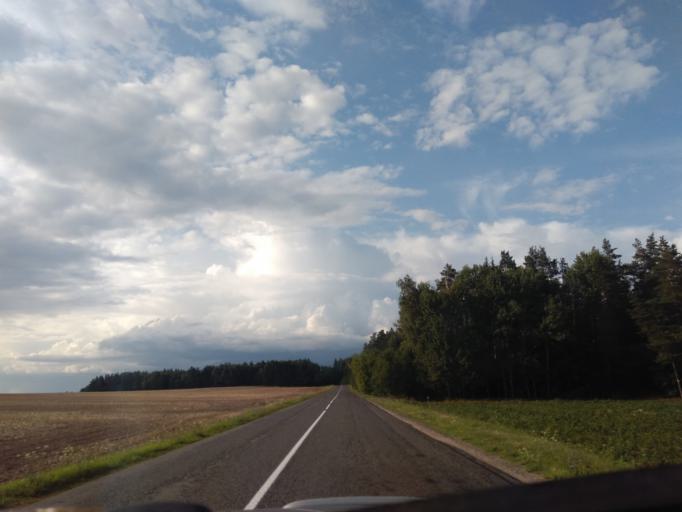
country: BY
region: Minsk
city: Kapyl'
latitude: 53.2887
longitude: 27.0805
